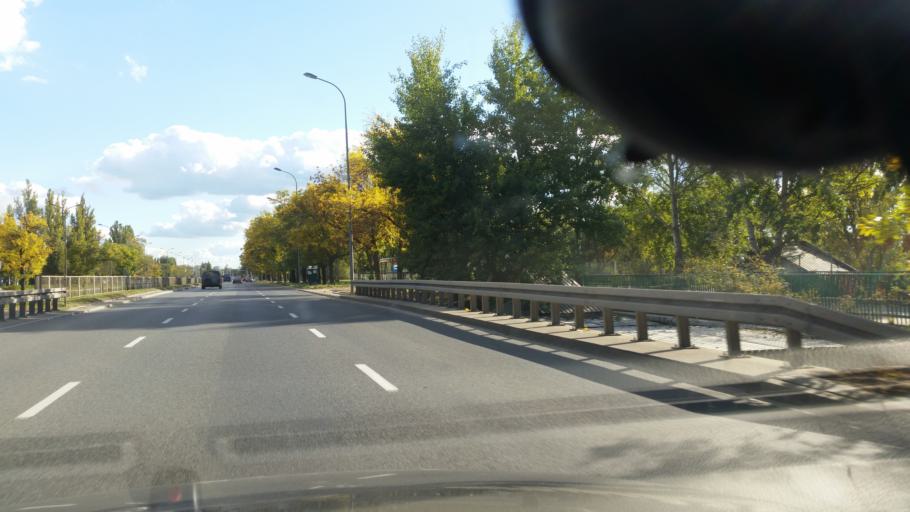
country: PL
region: Masovian Voivodeship
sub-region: Warszawa
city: Zoliborz
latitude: 52.2825
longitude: 21.0094
